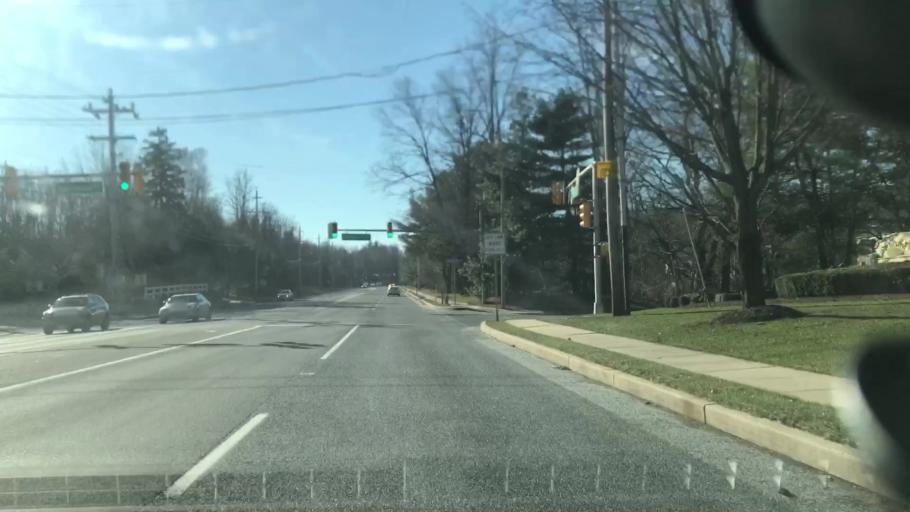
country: US
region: New Jersey
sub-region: Monmouth County
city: Keansburg
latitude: 40.3946
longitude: -74.1448
